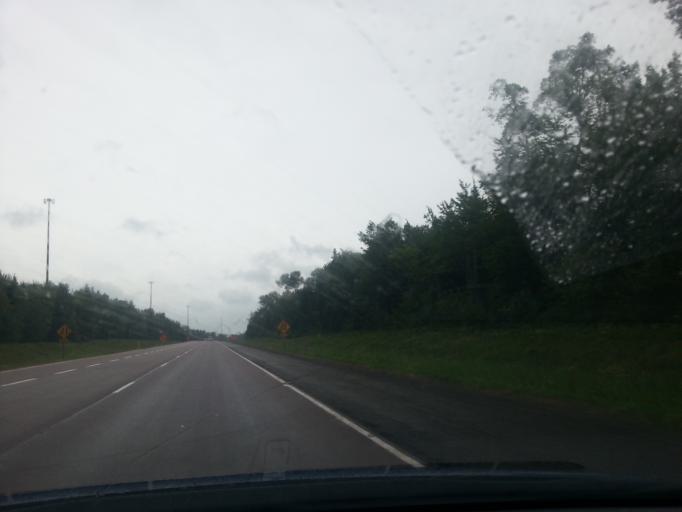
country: CA
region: New Brunswick
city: Salisbury
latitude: 45.9862
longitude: -65.1358
